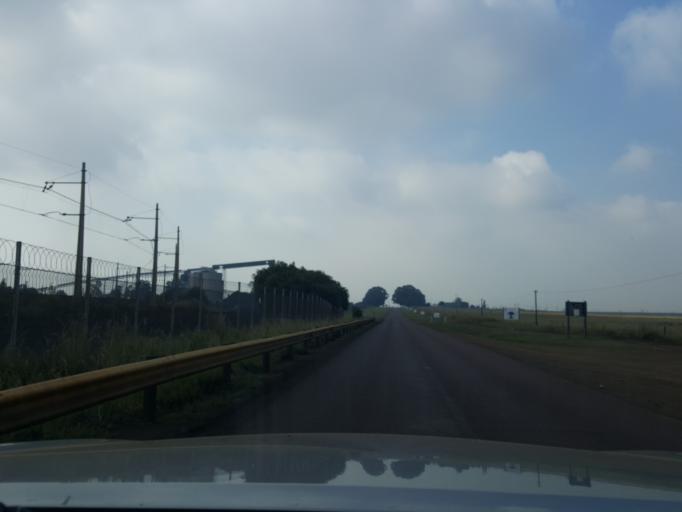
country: ZA
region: Mpumalanga
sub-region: Nkangala District Municipality
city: Middelburg
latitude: -25.9725
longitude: 29.4499
